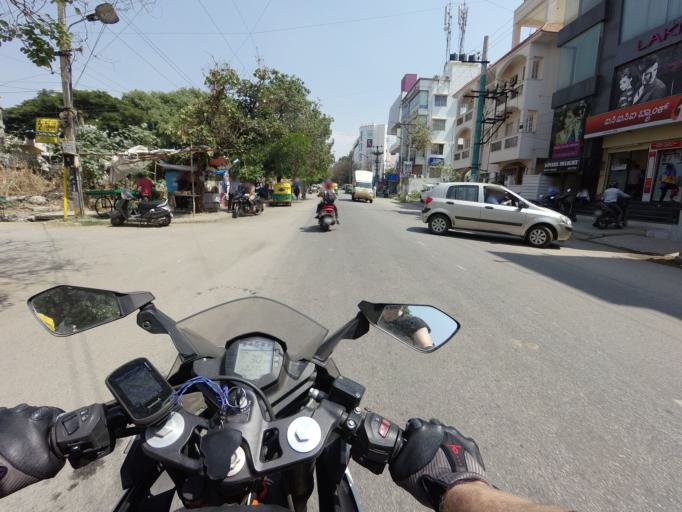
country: IN
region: Karnataka
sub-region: Bangalore Urban
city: Bangalore
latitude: 13.0071
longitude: 77.6590
